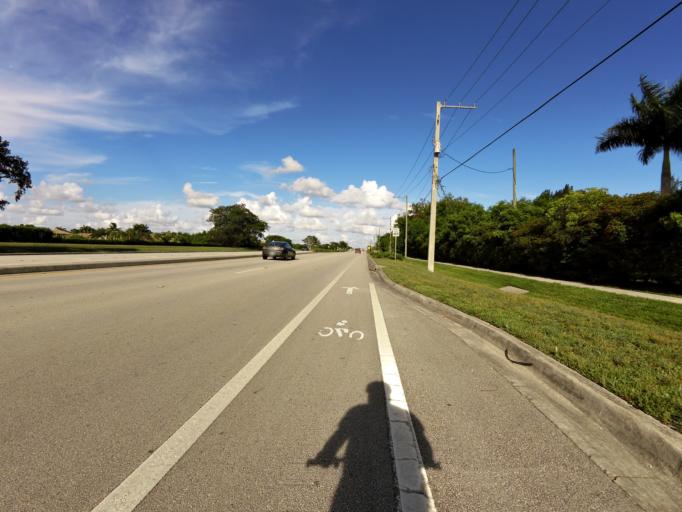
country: US
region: Florida
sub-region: Broward County
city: Southwest Ranches
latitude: 26.0622
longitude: -80.3731
